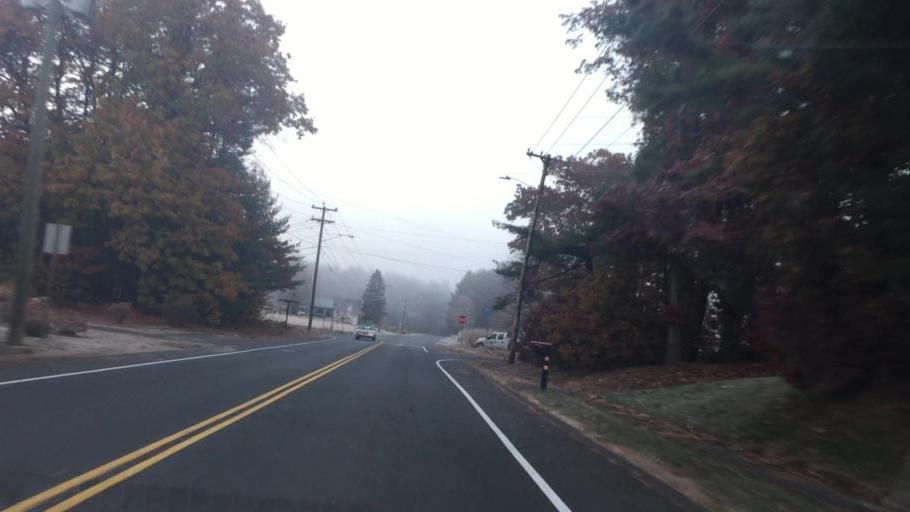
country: US
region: Massachusetts
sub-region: Hampshire County
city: Southampton
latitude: 42.2123
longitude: -72.6903
